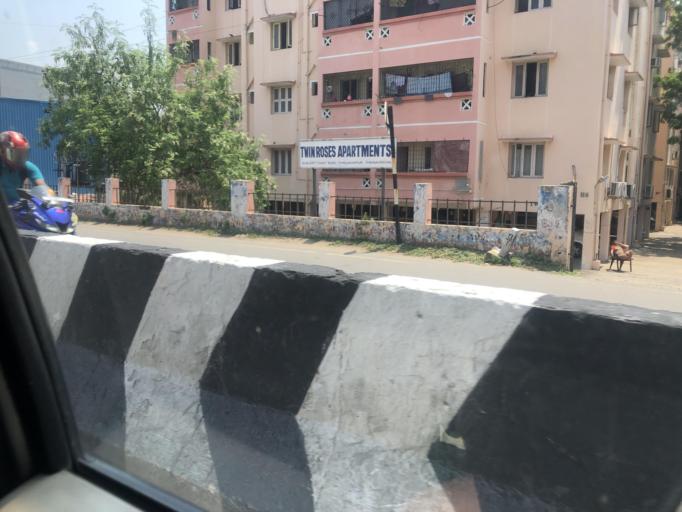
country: IN
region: Tamil Nadu
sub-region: Kancheepuram
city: Perungudi
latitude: 12.9800
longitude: 80.2593
